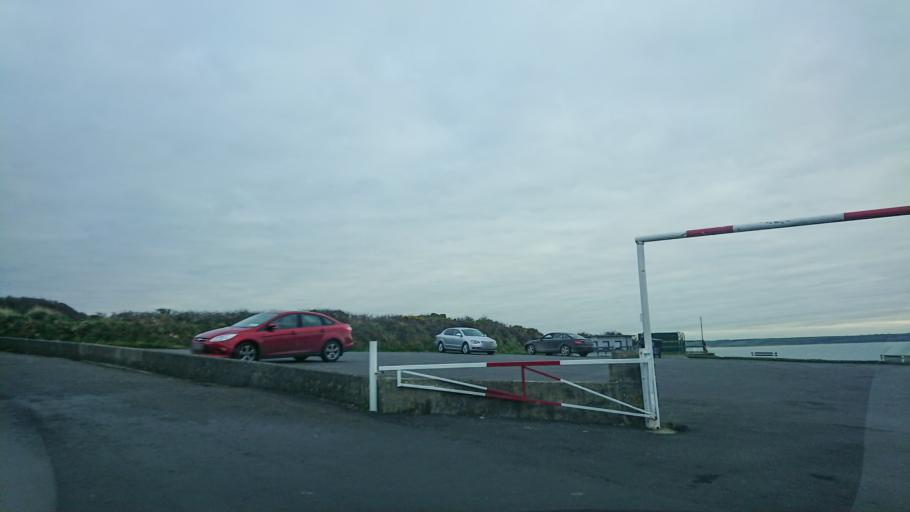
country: IE
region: Munster
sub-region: Waterford
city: Tra Mhor
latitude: 52.1437
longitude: -7.1664
